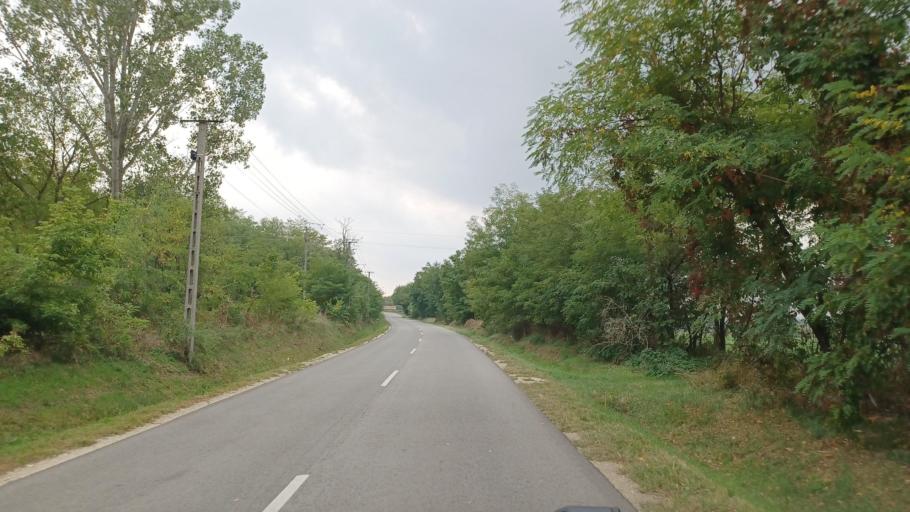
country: HU
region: Tolna
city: Pincehely
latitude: 46.6559
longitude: 18.4136
